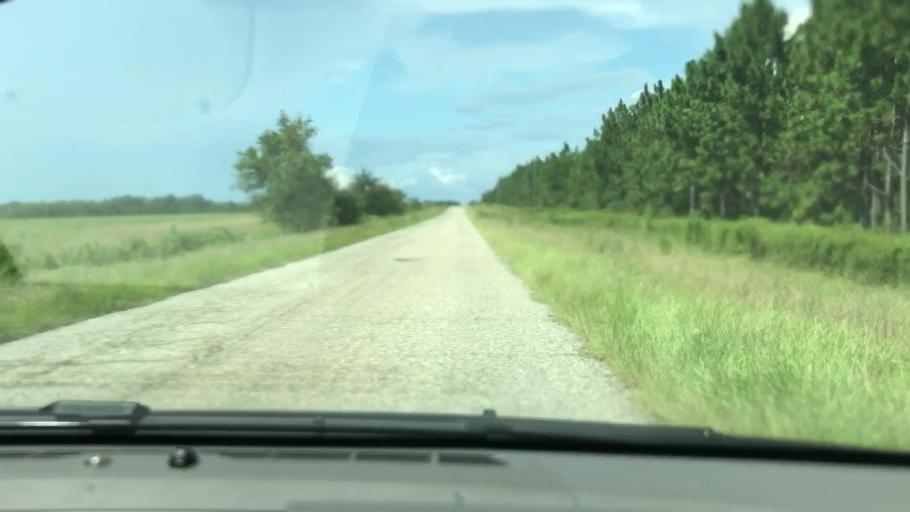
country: US
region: Georgia
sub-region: Seminole County
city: Donalsonville
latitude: 31.1739
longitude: -85.0046
